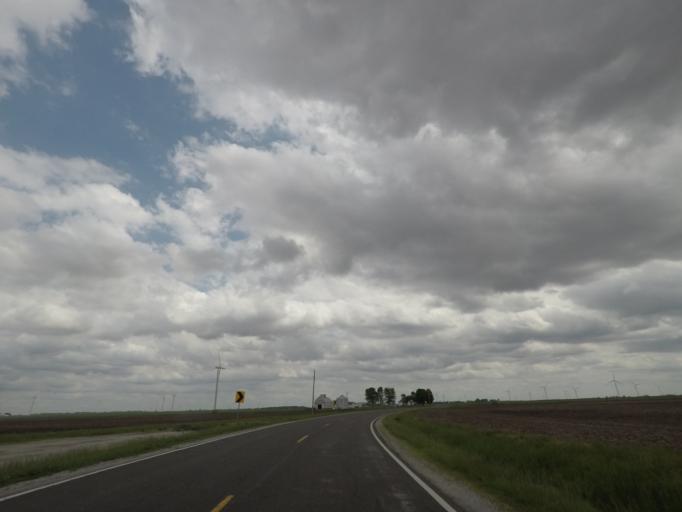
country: US
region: Illinois
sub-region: Macon County
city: Warrensburg
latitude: 40.0491
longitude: -89.0859
